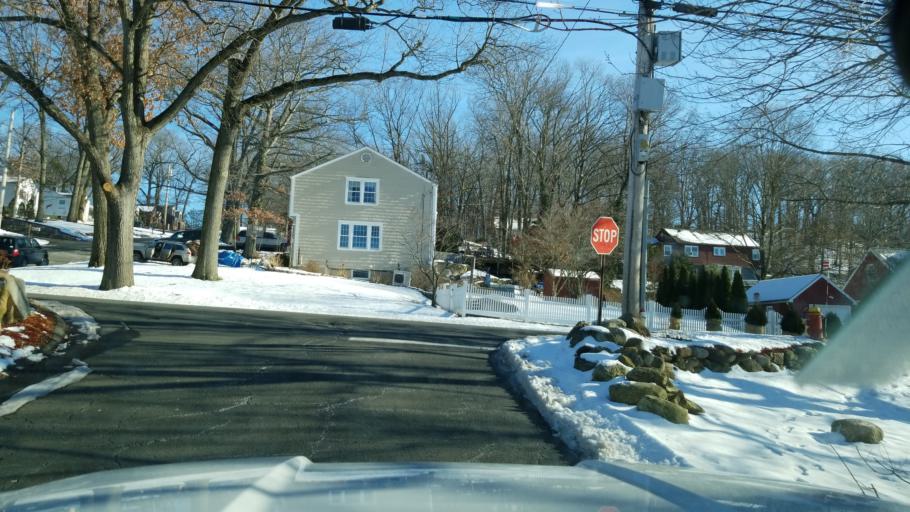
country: US
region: Connecticut
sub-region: New Haven County
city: Wallingford Center
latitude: 41.4408
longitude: -72.8305
